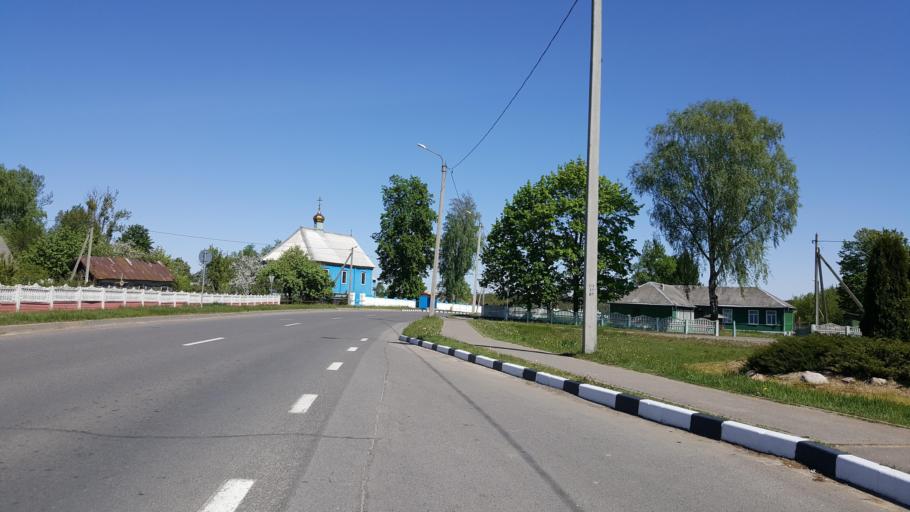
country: BY
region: Brest
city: Kamyanyuki
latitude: 52.4904
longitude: 23.7782
